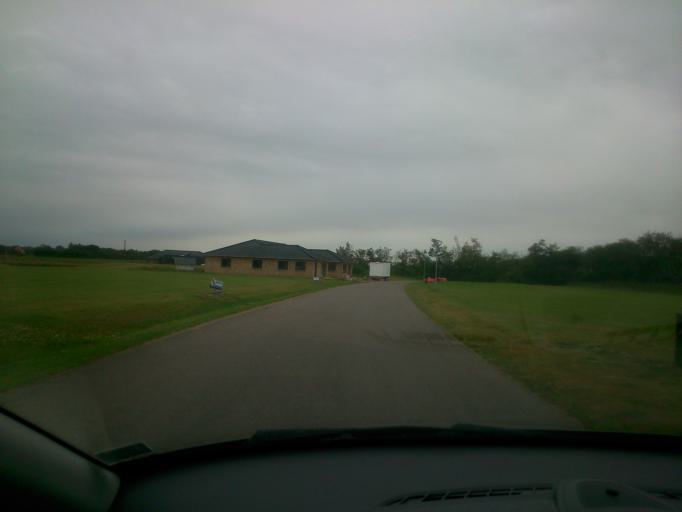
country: DK
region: Central Jutland
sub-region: Ringkobing-Skjern Kommune
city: Skjern
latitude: 55.9598
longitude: 8.4790
